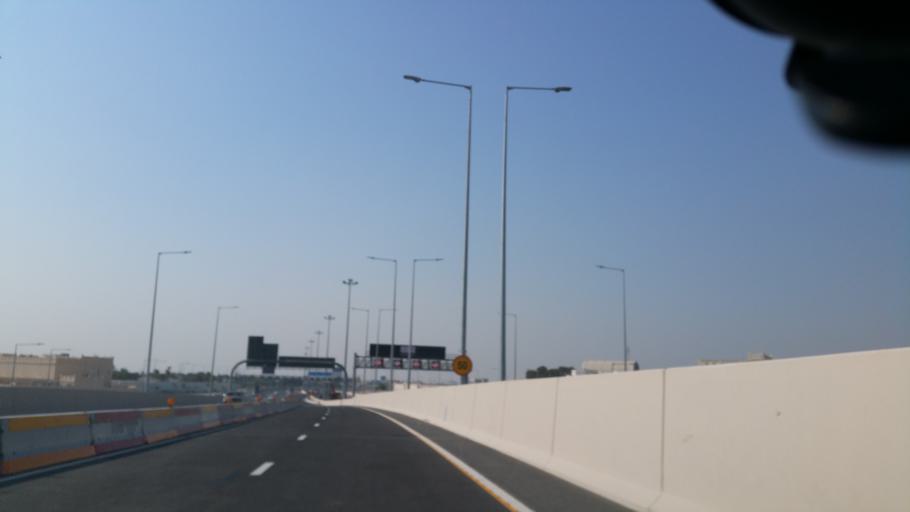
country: QA
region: Baladiyat ar Rayyan
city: Ar Rayyan
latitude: 25.2811
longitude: 51.4709
